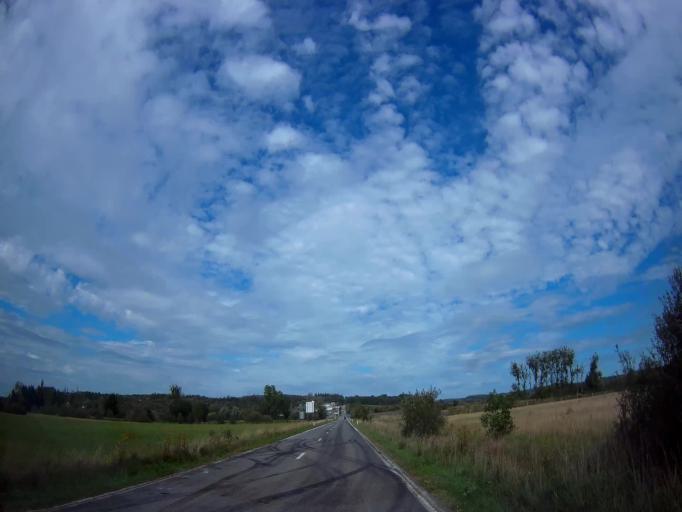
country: BE
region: Wallonia
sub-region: Province du Luxembourg
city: Hotton
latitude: 50.2769
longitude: 5.4536
